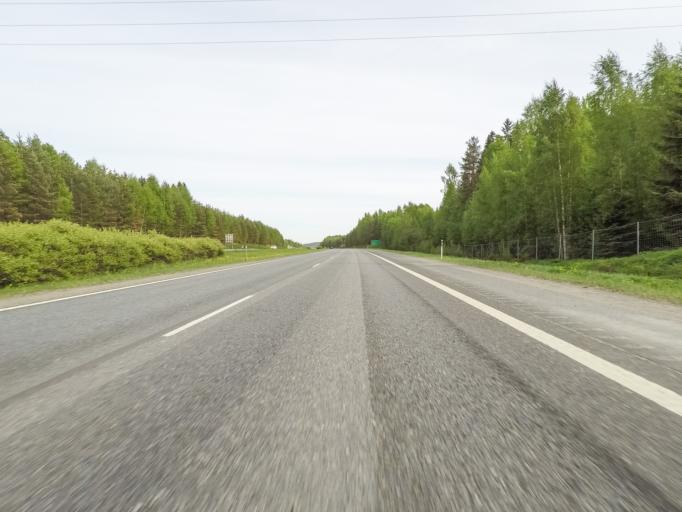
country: FI
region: Haeme
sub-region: Haemeenlinna
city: Parola
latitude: 61.0415
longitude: 24.3684
